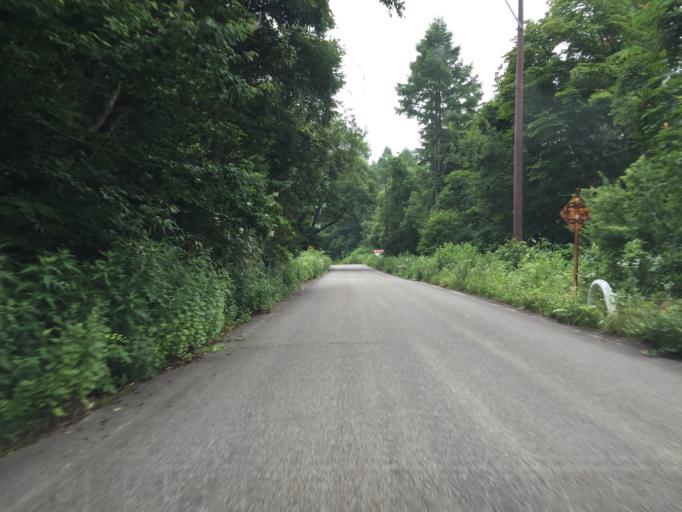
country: JP
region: Fukushima
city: Inawashiro
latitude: 37.6474
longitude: 140.2182
